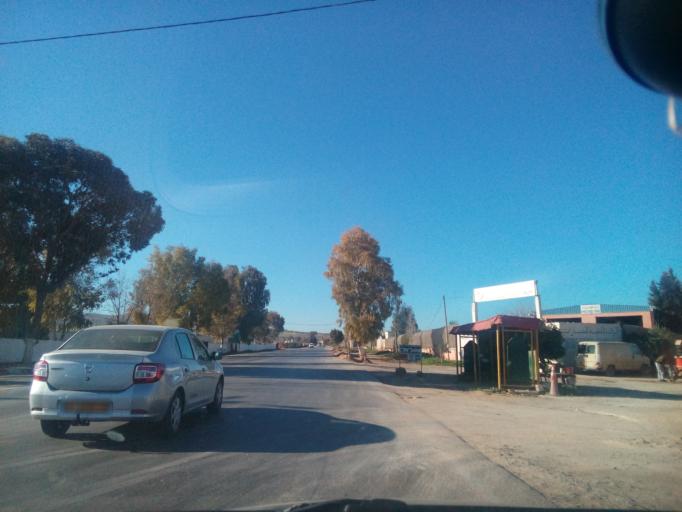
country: DZ
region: Relizane
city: Relizane
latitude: 35.9008
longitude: 0.5290
